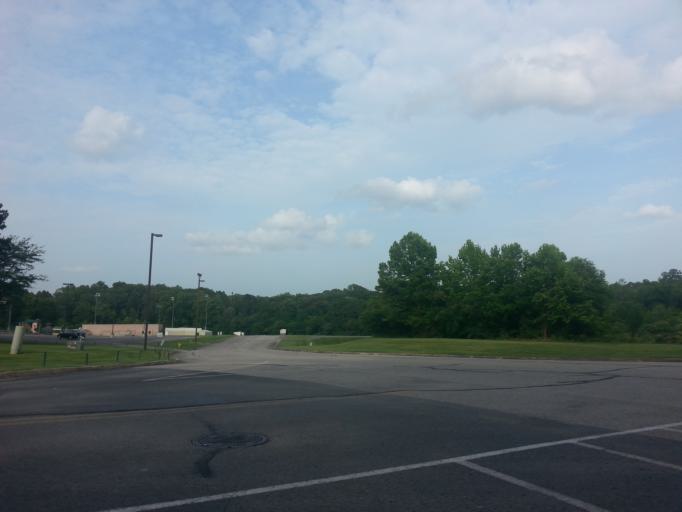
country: US
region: Tennessee
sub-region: Knox County
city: Knoxville
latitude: 35.9016
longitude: -83.9518
